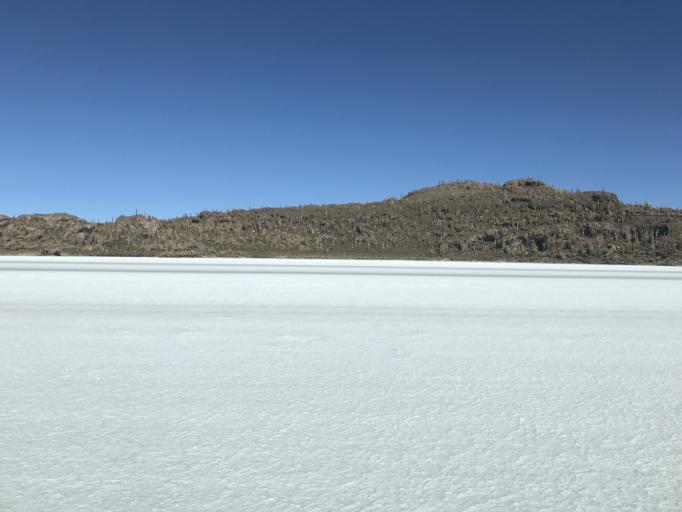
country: BO
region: Potosi
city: Colchani
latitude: -20.2386
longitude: -67.6257
